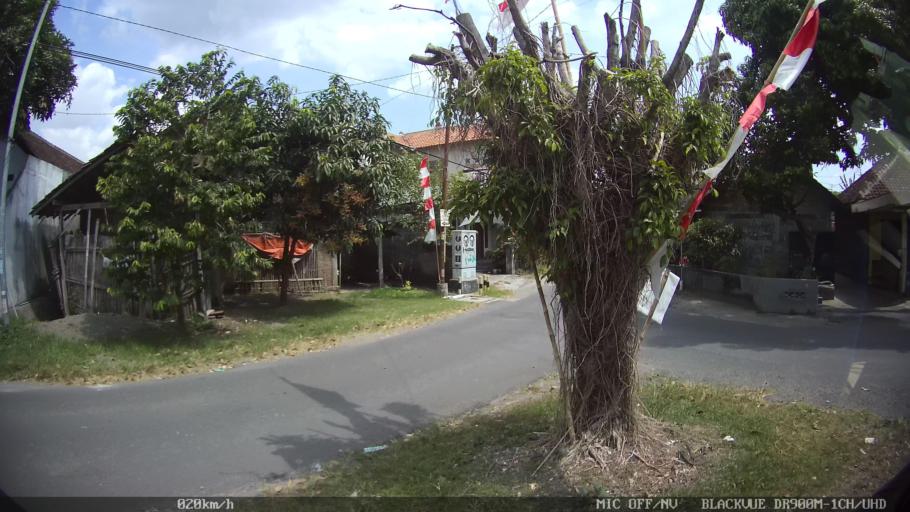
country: ID
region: Daerah Istimewa Yogyakarta
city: Kasihan
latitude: -7.8196
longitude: 110.3402
